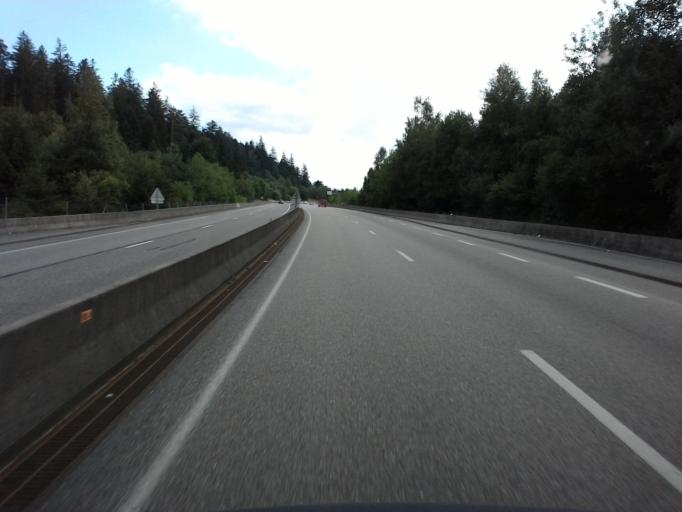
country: FR
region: Lorraine
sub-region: Departement des Vosges
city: Remiremont
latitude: 48.0072
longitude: 6.5578
